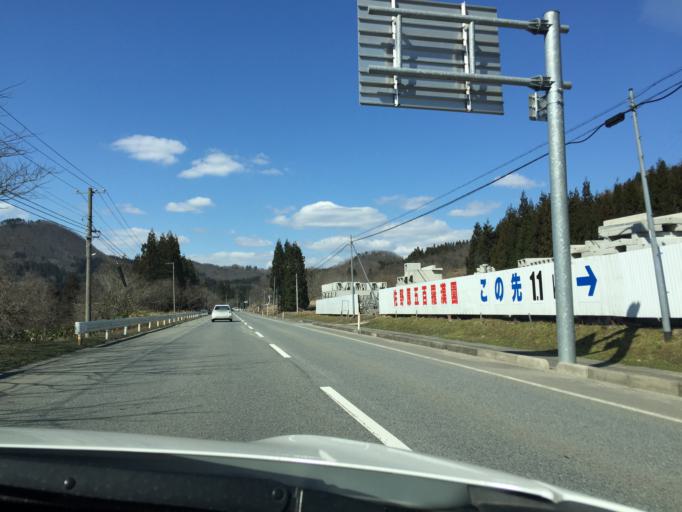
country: JP
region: Yamagata
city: Nagai
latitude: 38.2340
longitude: 140.0906
